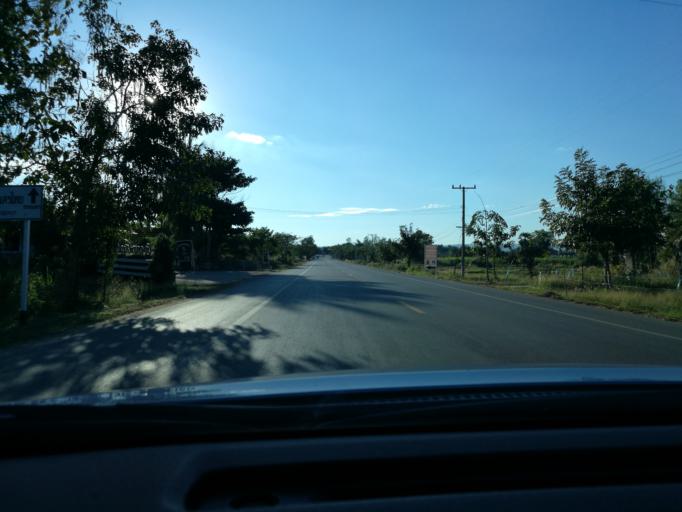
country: TH
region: Phitsanulok
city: Nakhon Thai
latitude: 17.0676
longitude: 100.8160
